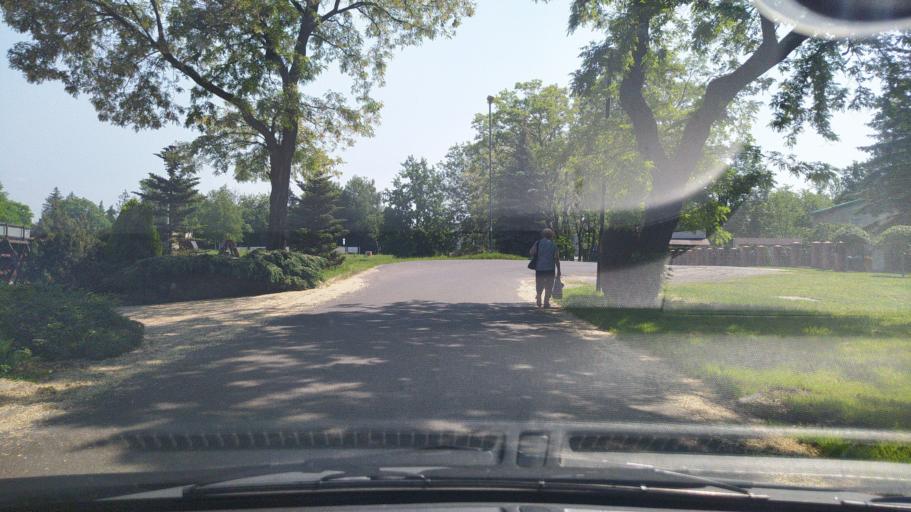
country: PL
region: Silesian Voivodeship
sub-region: Powiat gliwicki
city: Przyszowice
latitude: 50.2979
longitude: 18.7308
